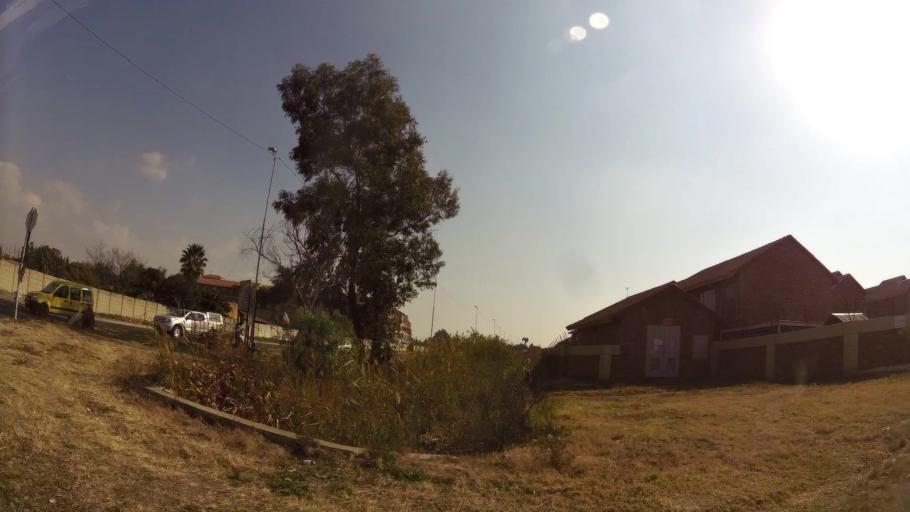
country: ZA
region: Gauteng
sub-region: Ekurhuleni Metropolitan Municipality
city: Boksburg
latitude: -26.1922
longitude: 28.2583
